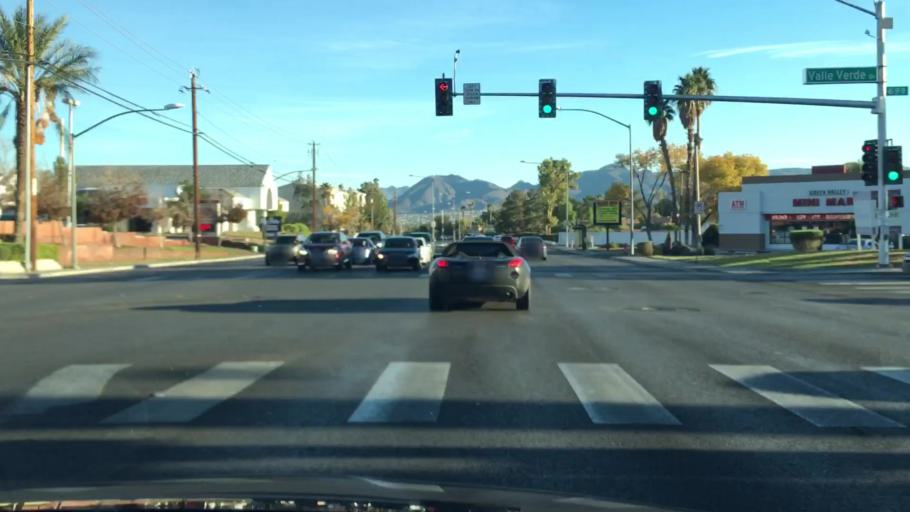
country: US
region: Nevada
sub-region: Clark County
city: Whitney
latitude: 36.0681
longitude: -115.0683
